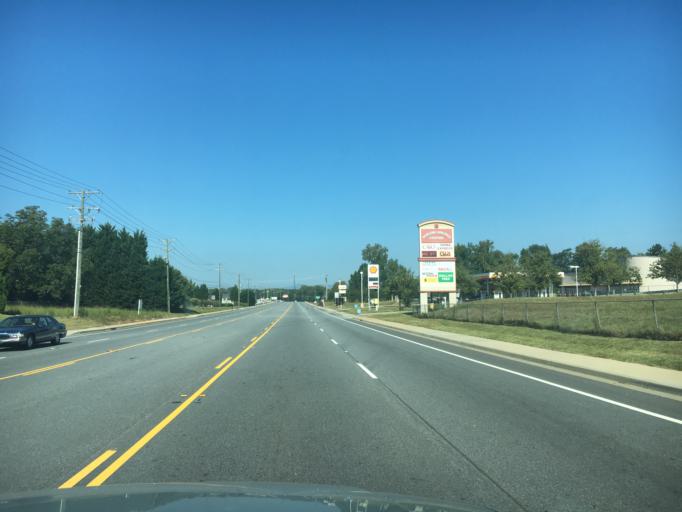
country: US
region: South Carolina
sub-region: Spartanburg County
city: Boiling Springs
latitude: 35.0510
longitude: -81.9880
